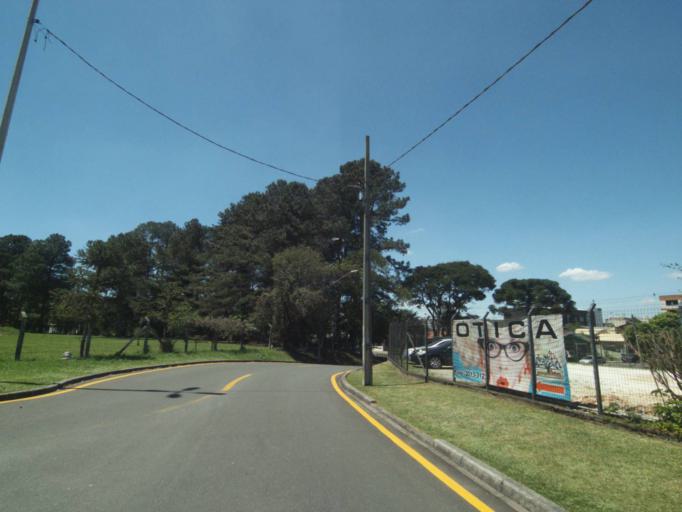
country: BR
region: Parana
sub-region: Curitiba
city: Curitiba
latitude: -25.3917
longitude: -49.2279
